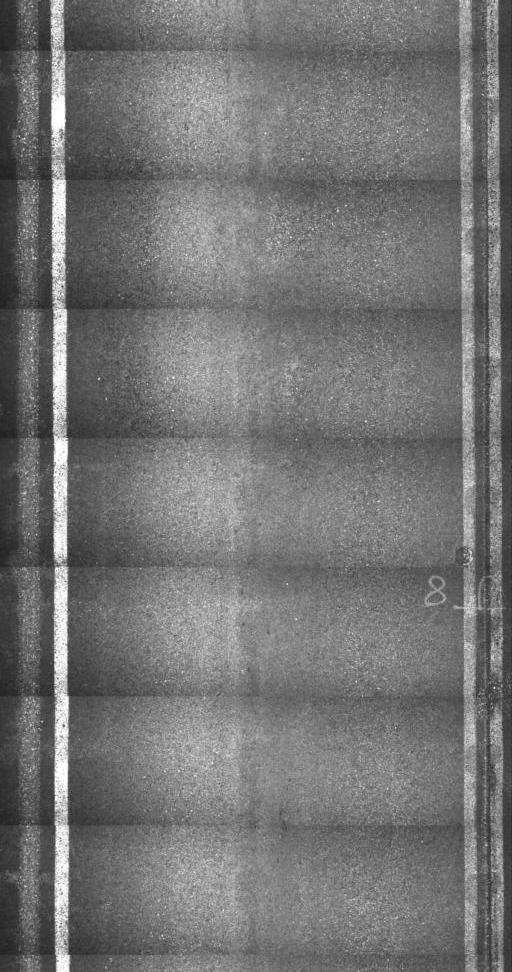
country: CA
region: Quebec
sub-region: Monteregie
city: Sutton
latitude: 44.9830
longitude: -72.4910
